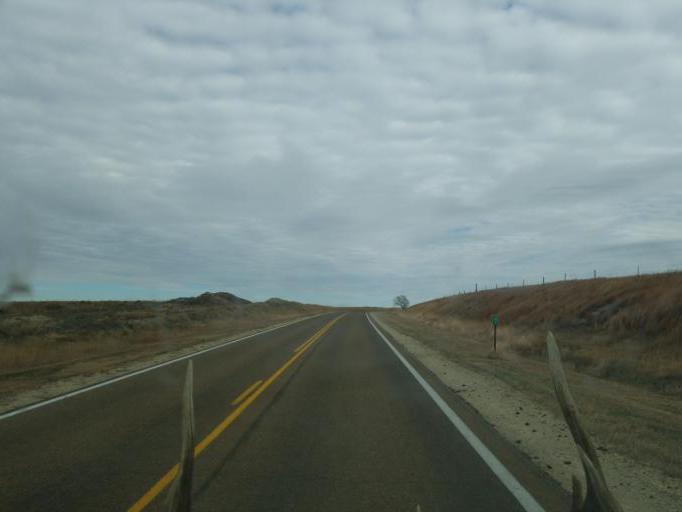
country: US
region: Kansas
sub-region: Wallace County
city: Sharon Springs
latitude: 39.0211
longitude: -101.3400
